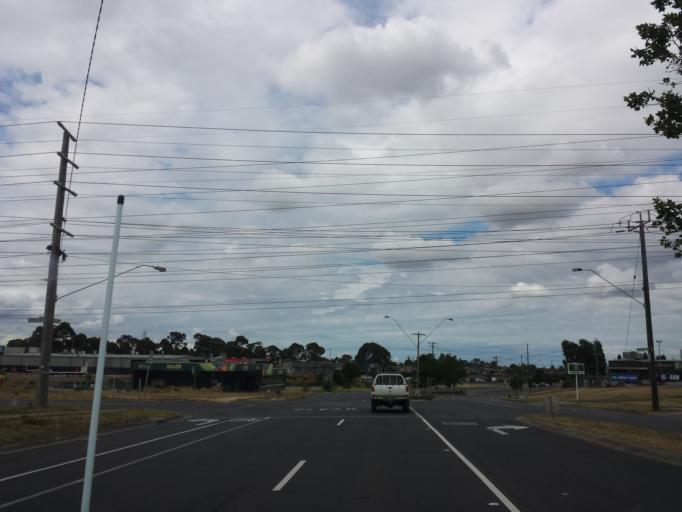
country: AU
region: Victoria
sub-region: Whittlesea
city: Thomastown
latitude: -37.6914
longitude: 145.0021
